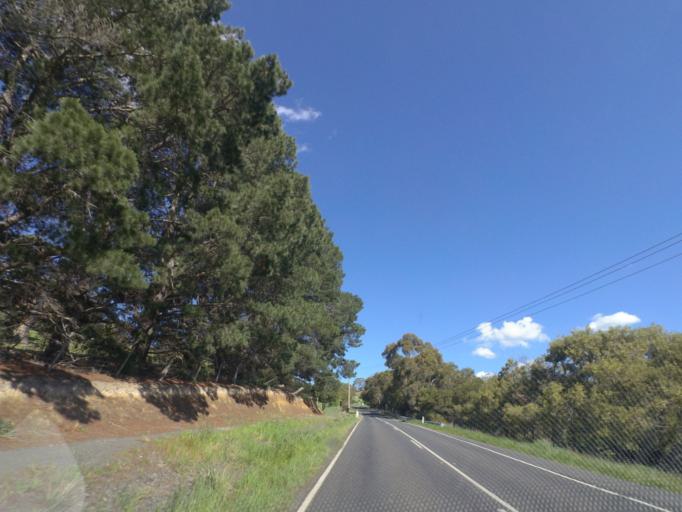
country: AU
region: Victoria
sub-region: Moorabool
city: Bacchus Marsh
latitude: -37.5649
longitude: 144.3078
